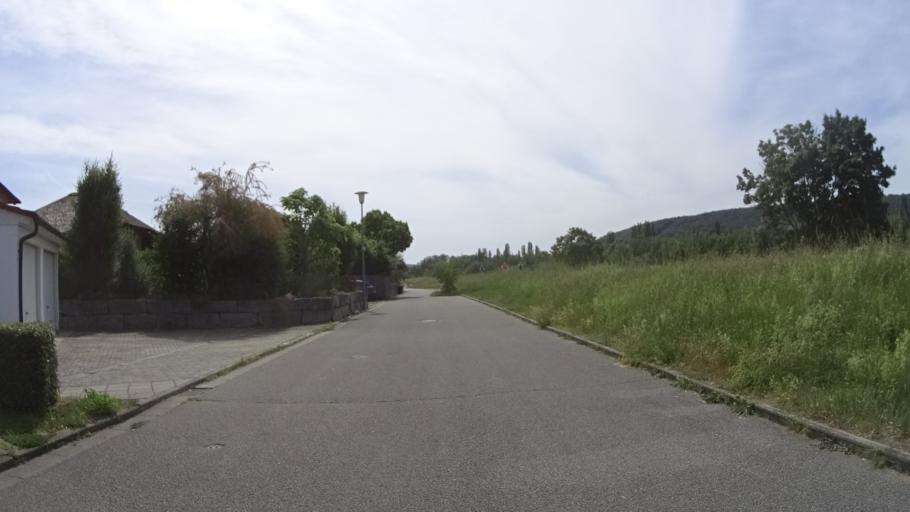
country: DE
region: Bavaria
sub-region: Lower Bavaria
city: Kelheim
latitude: 48.9145
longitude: 11.8825
